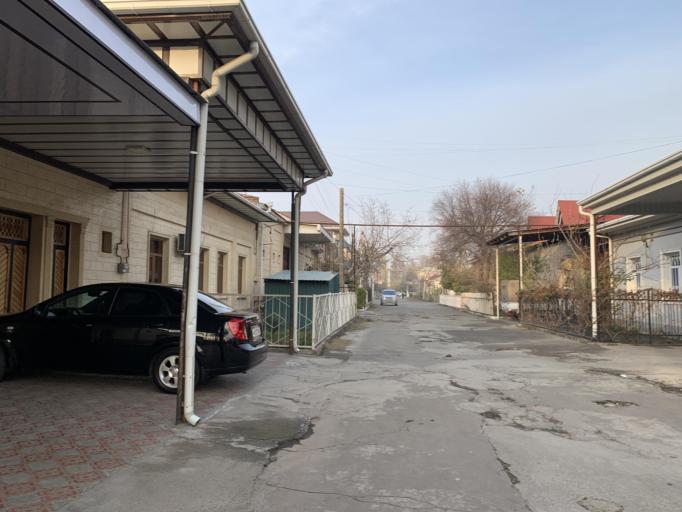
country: UZ
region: Fergana
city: Qo`qon
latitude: 40.5441
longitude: 70.9266
